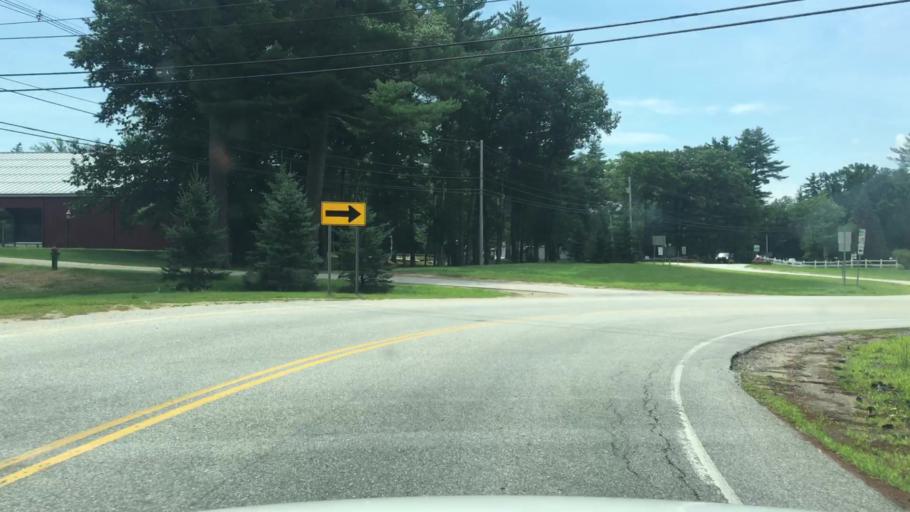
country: US
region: New Hampshire
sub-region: Grafton County
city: Plymouth
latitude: 43.7613
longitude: -71.6719
